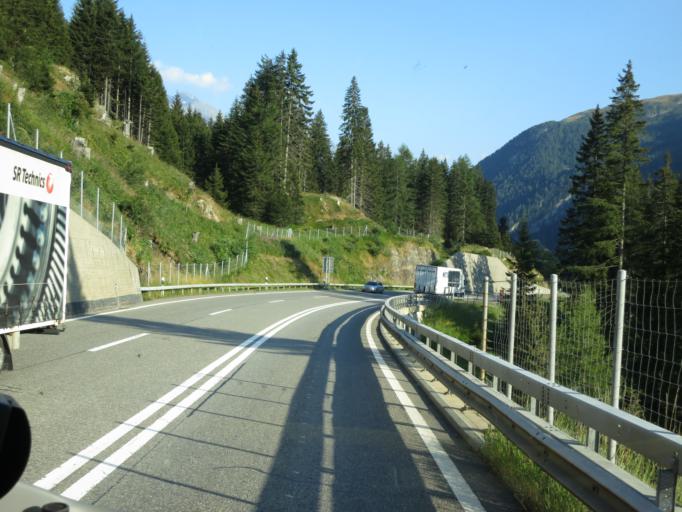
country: CH
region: Grisons
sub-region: Moesa District
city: Mesocco
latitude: 46.4402
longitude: 9.1922
